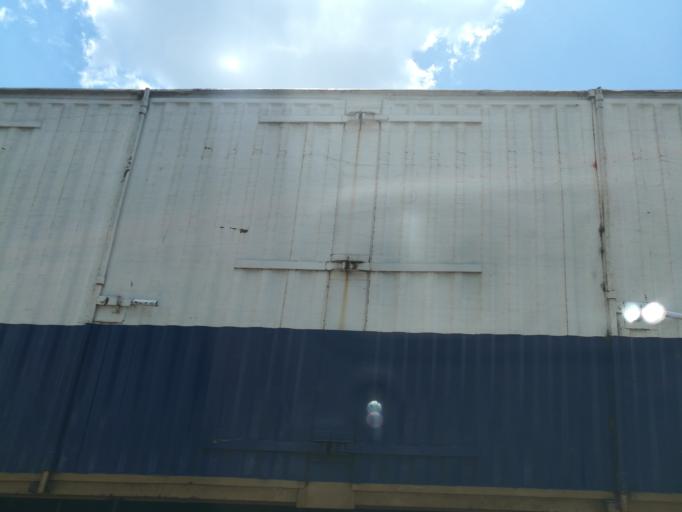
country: KE
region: Nairobi Area
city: Nairobi
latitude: -1.3190
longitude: 36.8167
